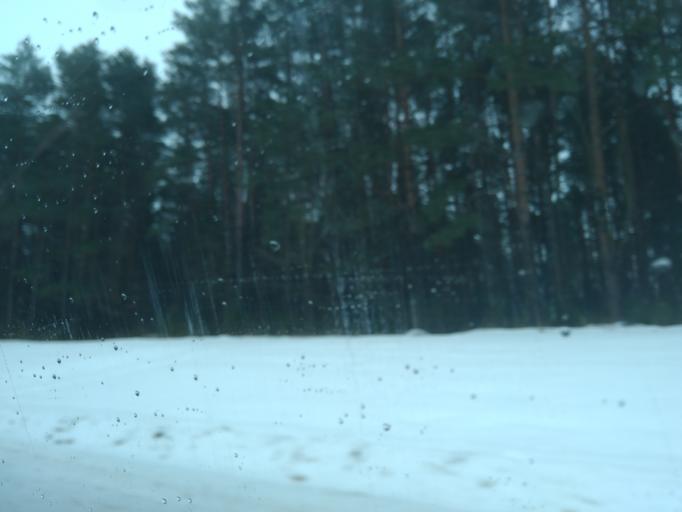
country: BY
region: Minsk
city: Stowbtsy
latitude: 53.5656
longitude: 26.7848
